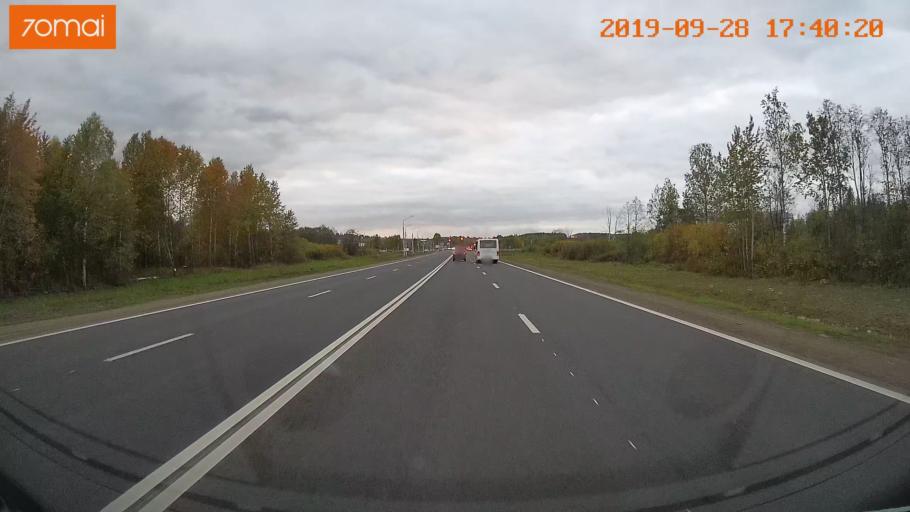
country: RU
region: Jaroslavl
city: Yaroslavl
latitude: 57.5494
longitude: 39.8970
